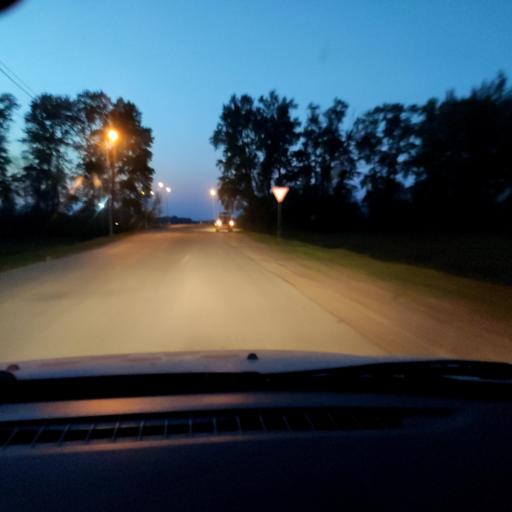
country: RU
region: Bashkortostan
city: Karmaskaly
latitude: 54.3832
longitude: 56.1519
